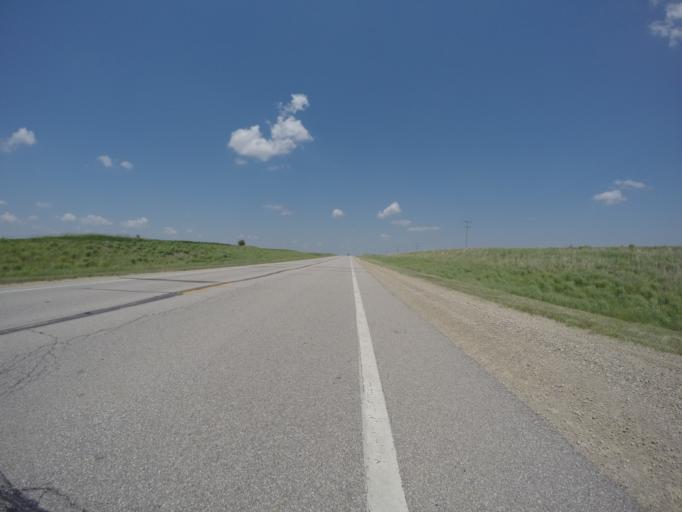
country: US
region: Kansas
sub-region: Doniphan County
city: Troy
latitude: 39.7464
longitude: -95.1438
